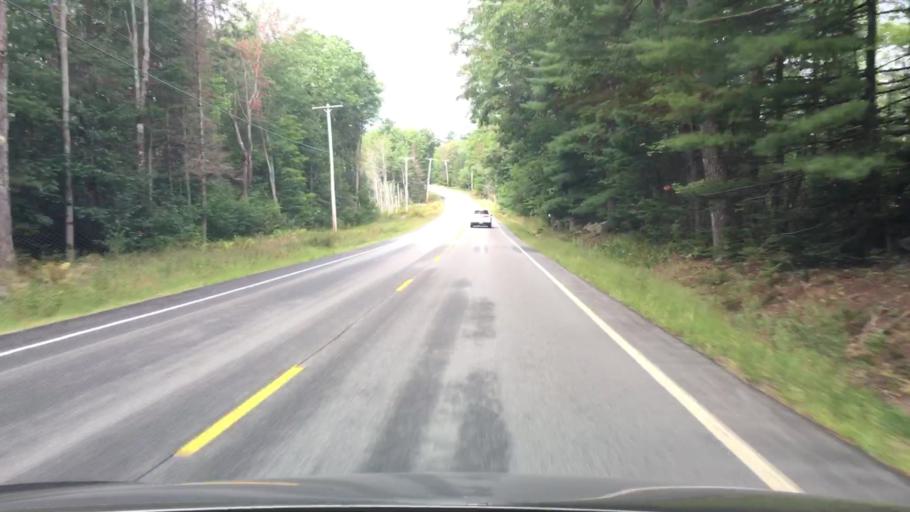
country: US
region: Maine
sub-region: Oxford County
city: Hartford
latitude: 44.3658
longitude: -70.3352
